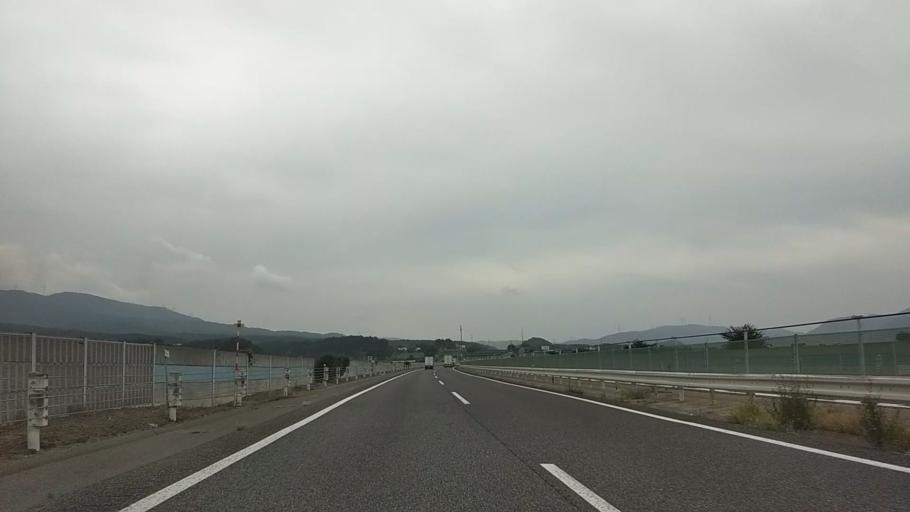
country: JP
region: Nagano
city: Shiojiri
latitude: 36.1314
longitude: 137.9728
